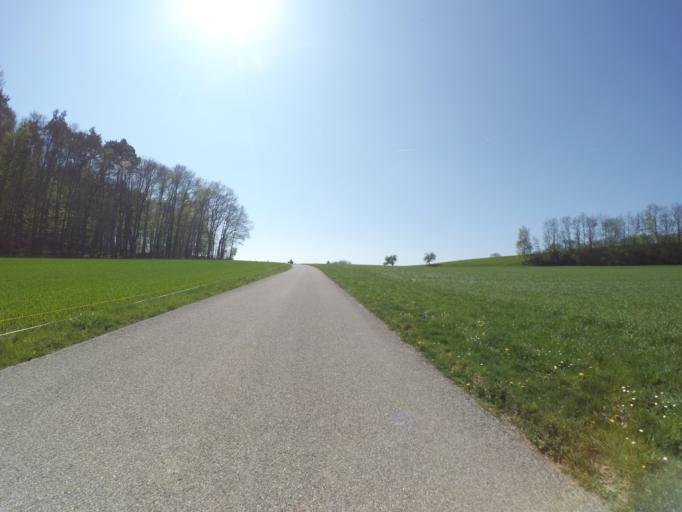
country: CH
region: Thurgau
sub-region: Frauenfeld District
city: Diessenhofen
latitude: 47.6319
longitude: 8.7375
